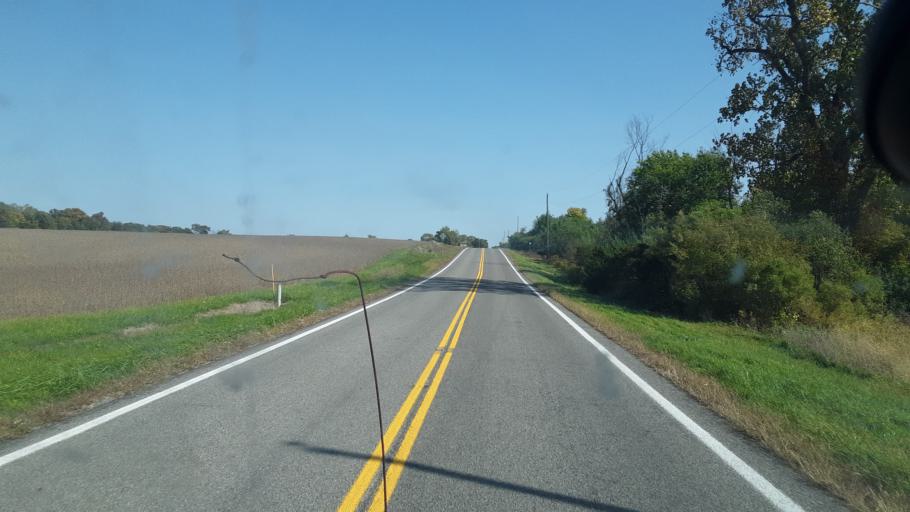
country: US
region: Ohio
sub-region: Logan County
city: Northwood
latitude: 40.5059
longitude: -83.6761
